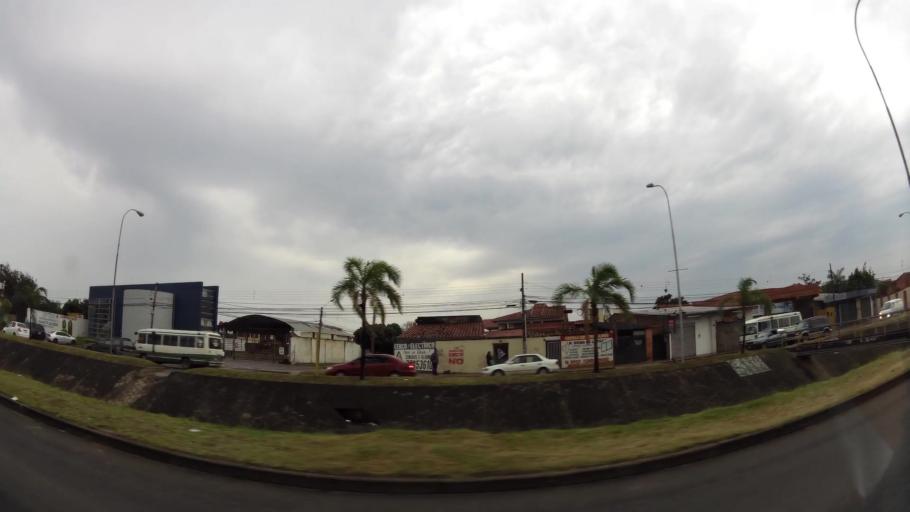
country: BO
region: Santa Cruz
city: Santa Cruz de la Sierra
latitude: -17.7807
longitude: -63.1494
